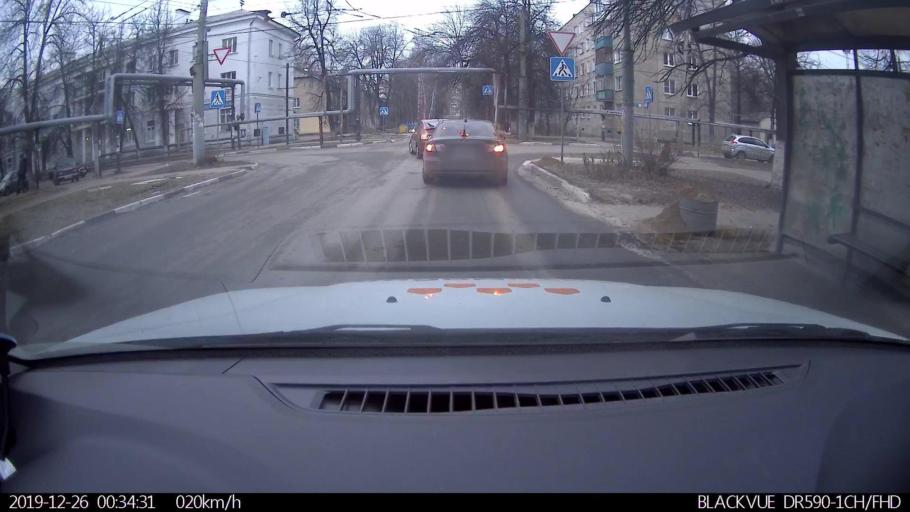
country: RU
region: Nizjnij Novgorod
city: Nizhniy Novgorod
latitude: 56.2898
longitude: 43.9159
